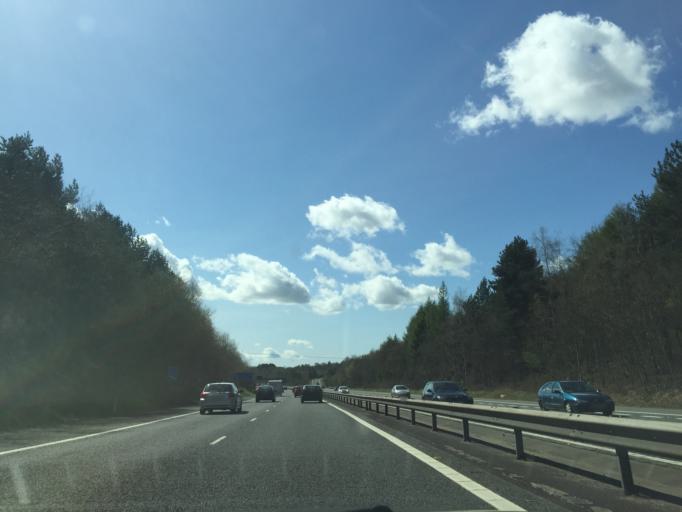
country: GB
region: England
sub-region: Hampshire
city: Cowplain
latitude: 50.8814
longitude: -1.0088
